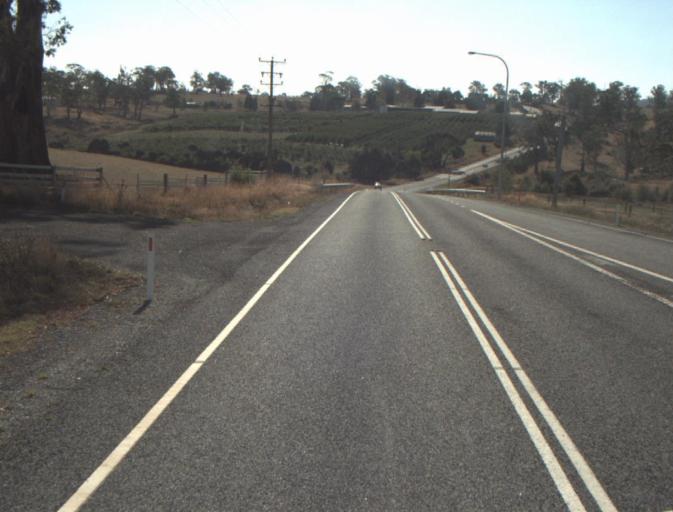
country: AU
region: Tasmania
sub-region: Launceston
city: Mayfield
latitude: -41.3509
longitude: 147.0985
